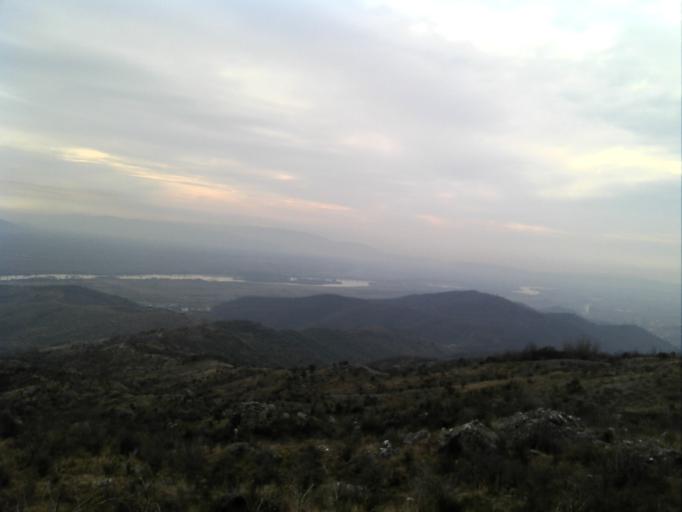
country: AL
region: Shkoder
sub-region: Rrethi i Shkodres
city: Berdica e Madhe
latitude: 42.0387
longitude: 19.4552
